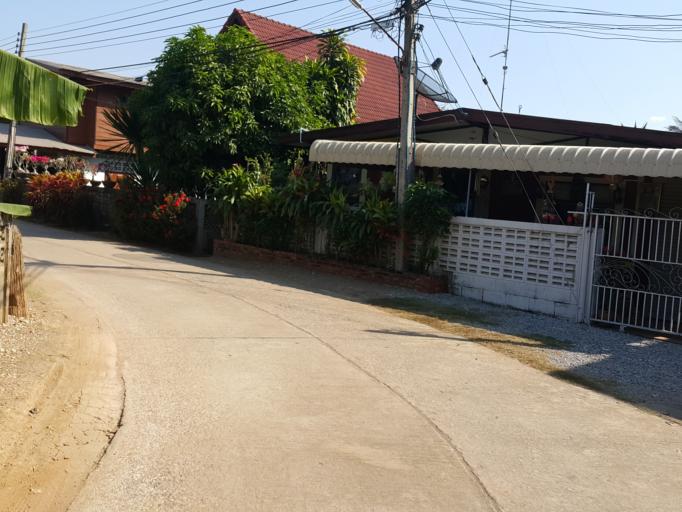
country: TH
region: Sukhothai
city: Thung Saliam
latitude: 17.3169
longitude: 99.5578
